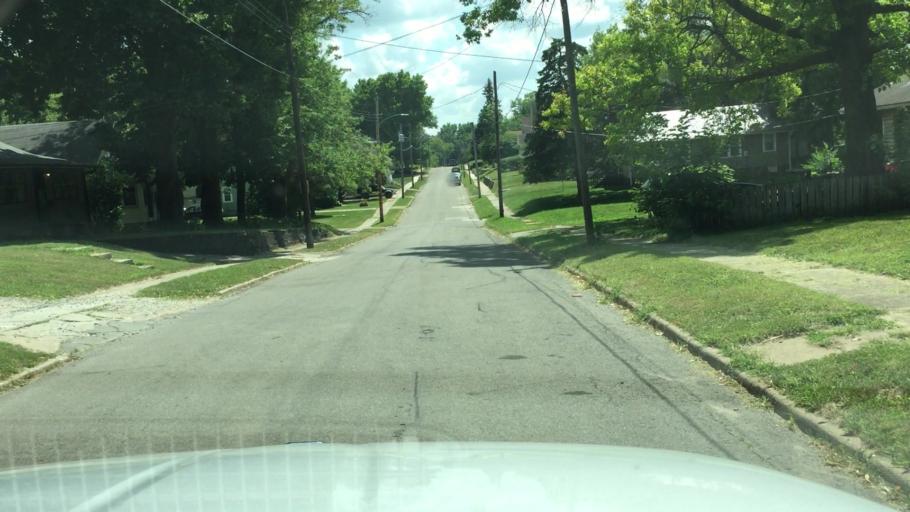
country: US
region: Iowa
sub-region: Jasper County
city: Newton
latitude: 41.6952
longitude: -93.0549
